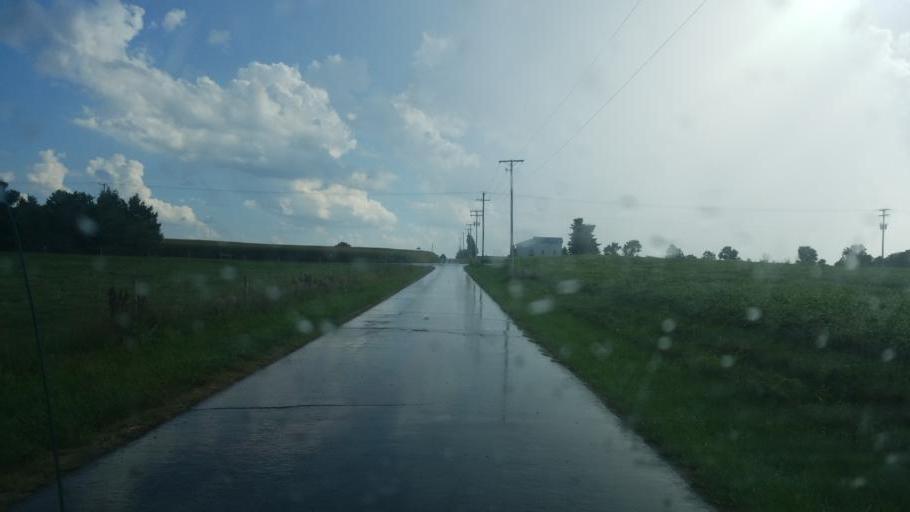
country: US
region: Ohio
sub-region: Huron County
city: Greenwich
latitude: 40.9951
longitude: -82.5585
